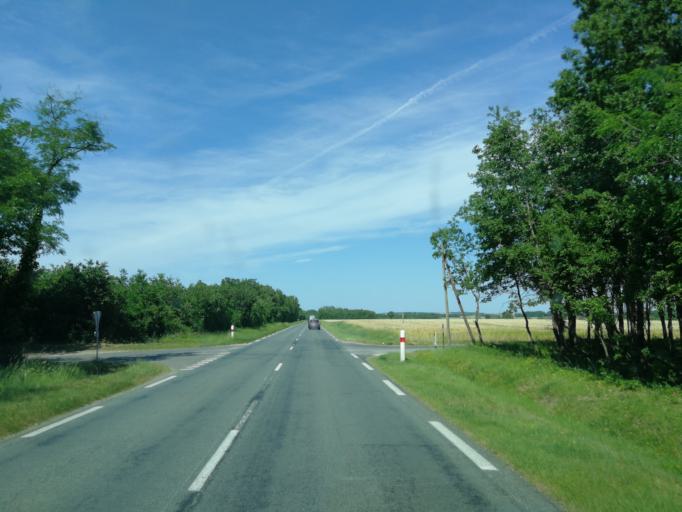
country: FR
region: Poitou-Charentes
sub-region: Departement de la Vienne
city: Loudun
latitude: 47.0550
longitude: 0.1487
